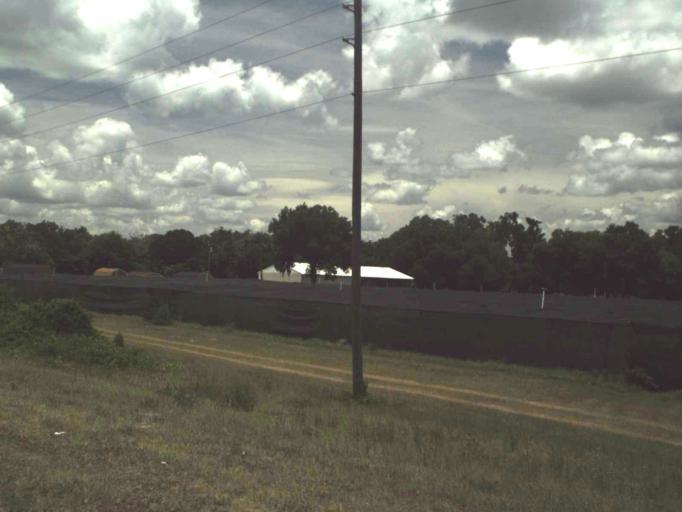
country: US
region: Florida
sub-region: Volusia County
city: West DeLand
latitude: 29.0276
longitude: -81.3421
